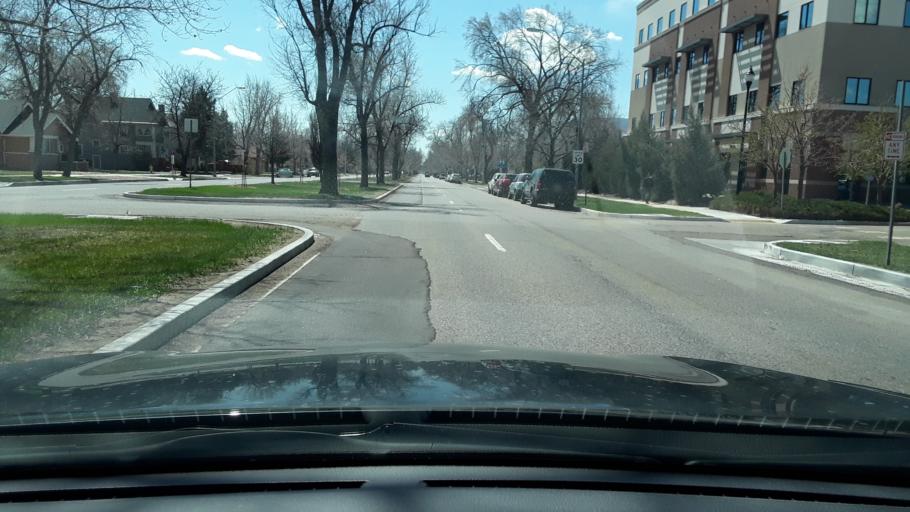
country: US
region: Colorado
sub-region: El Paso County
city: Colorado Springs
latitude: 38.8664
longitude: -104.8201
